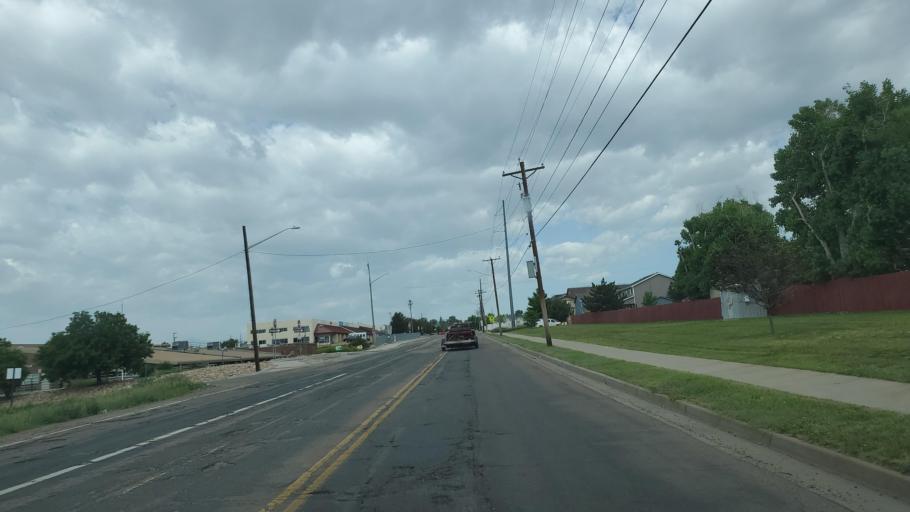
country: US
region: Colorado
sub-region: Adams County
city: Welby
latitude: 39.8382
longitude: -104.9727
